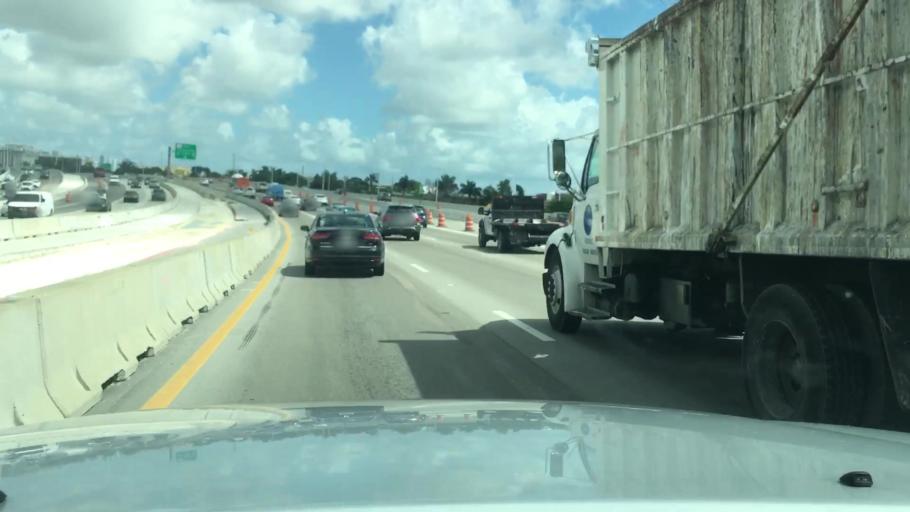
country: US
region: Florida
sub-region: Miami-Dade County
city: West Miami
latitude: 25.7845
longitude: -80.2731
